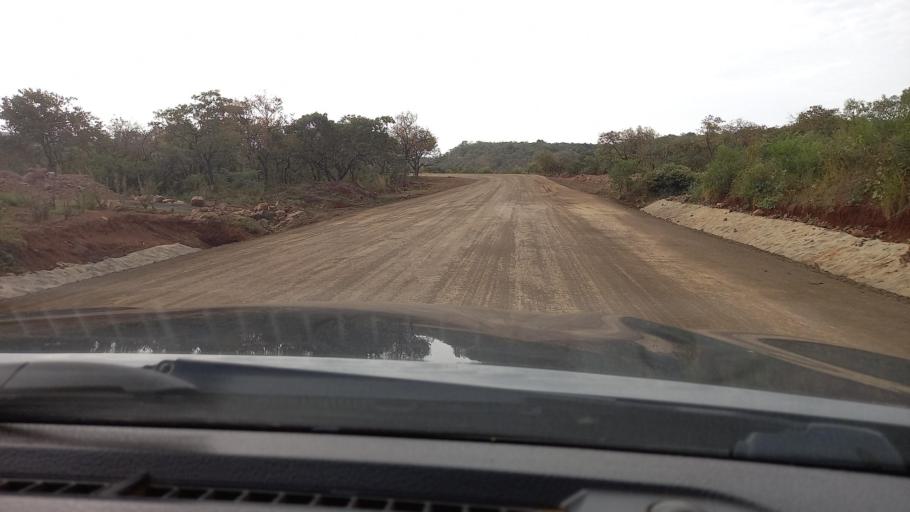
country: ET
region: Southern Nations, Nationalities, and People's Region
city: Mizan Teferi
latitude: 6.1898
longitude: 35.6862
